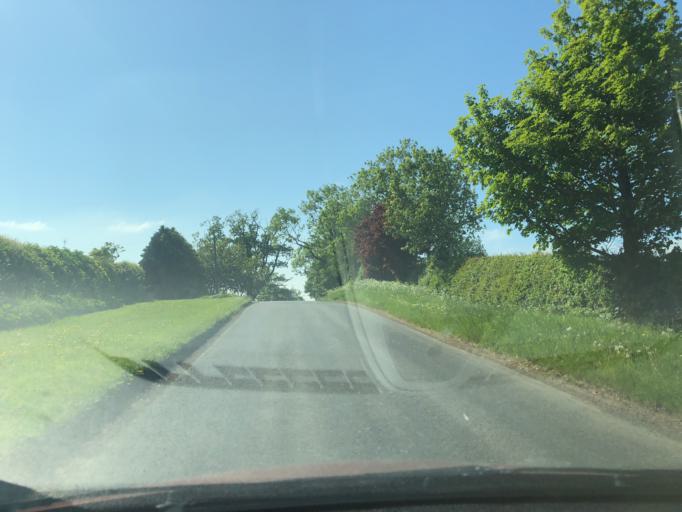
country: GB
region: England
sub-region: North Yorkshire
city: Northallerton
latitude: 54.3258
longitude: -1.3992
